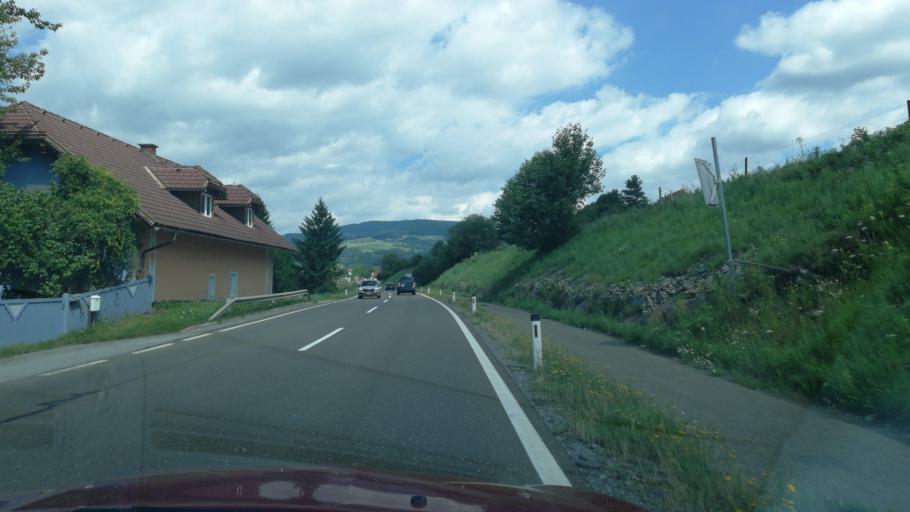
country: AT
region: Styria
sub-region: Politischer Bezirk Murau
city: Sankt Marein bei Neumarkt
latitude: 47.0570
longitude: 14.4331
